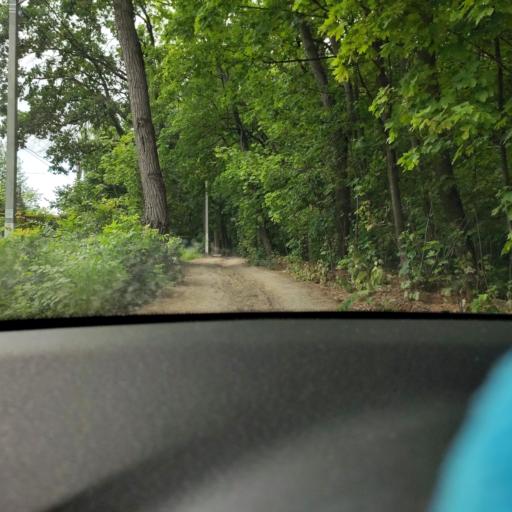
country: RU
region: Samara
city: Samara
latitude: 53.2958
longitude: 50.2296
